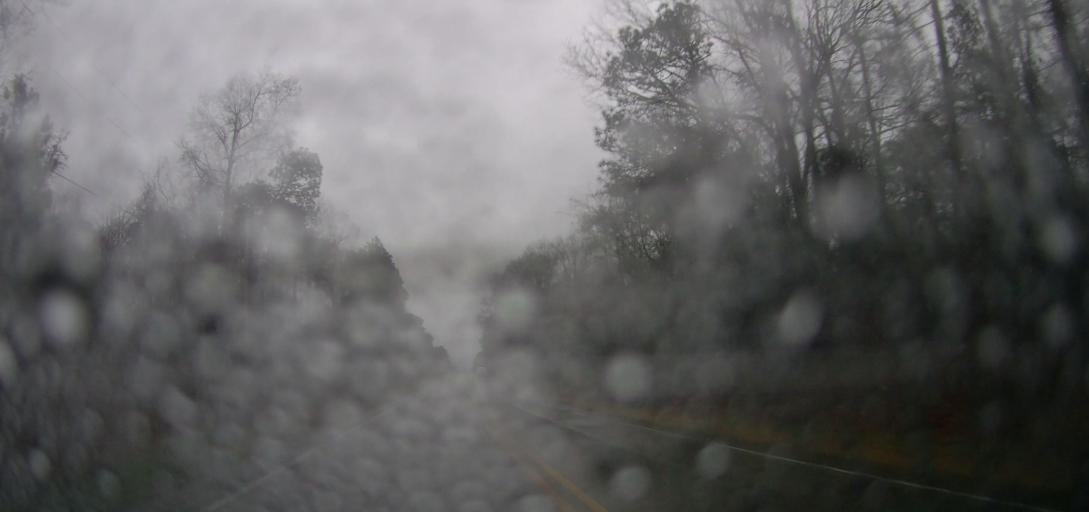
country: US
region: Alabama
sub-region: Autauga County
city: Pine Level
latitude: 32.5195
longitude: -86.6044
